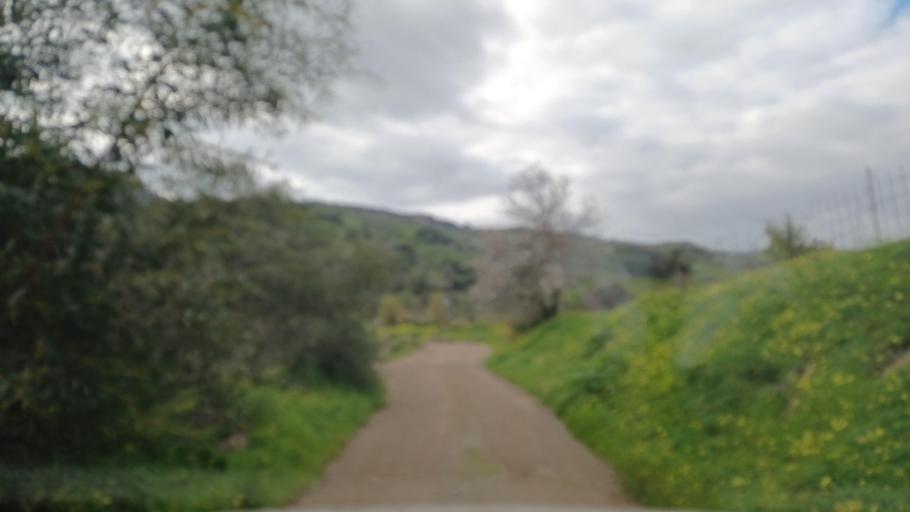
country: CY
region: Limassol
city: Pissouri
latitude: 34.7771
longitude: 32.6589
